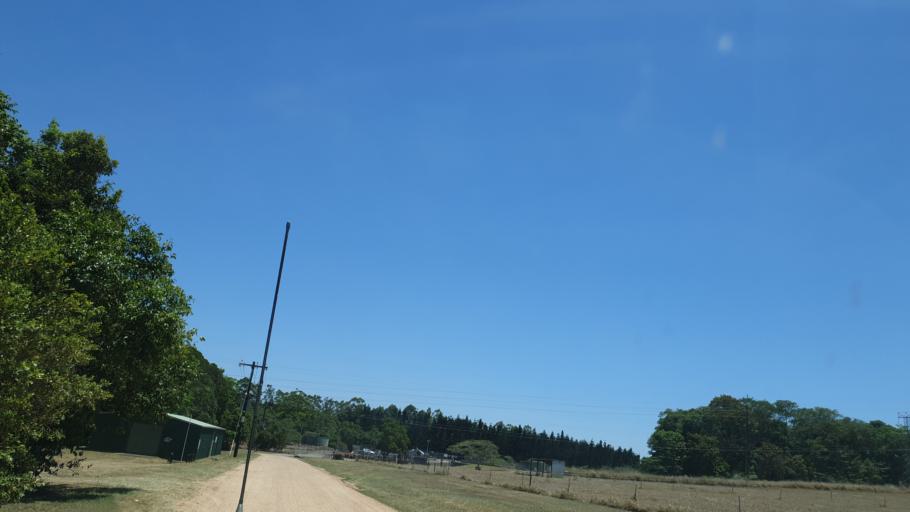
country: AU
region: Queensland
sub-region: Tablelands
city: Atherton
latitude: -17.2565
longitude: 145.4799
